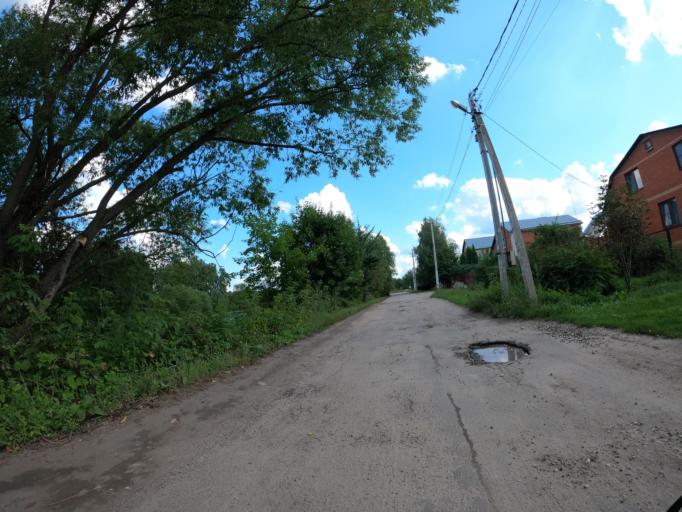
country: RU
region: Moskovskaya
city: Voskresensk
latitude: 55.2725
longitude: 38.6495
